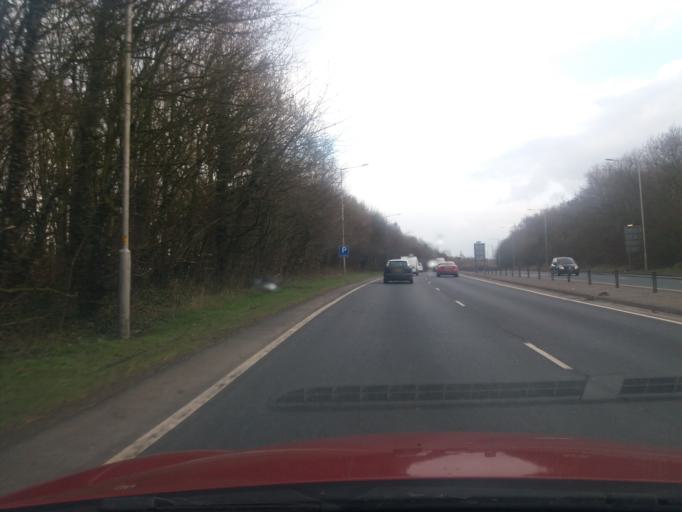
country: GB
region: England
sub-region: Lancashire
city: Leyland
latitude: 53.7411
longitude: -2.6804
